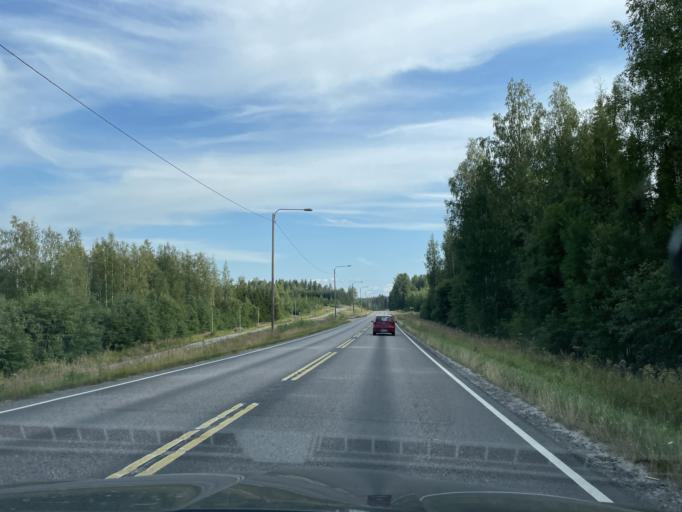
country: FI
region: Central Finland
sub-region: Jaemsae
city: Kuhmoinen
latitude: 61.5457
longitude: 25.1586
